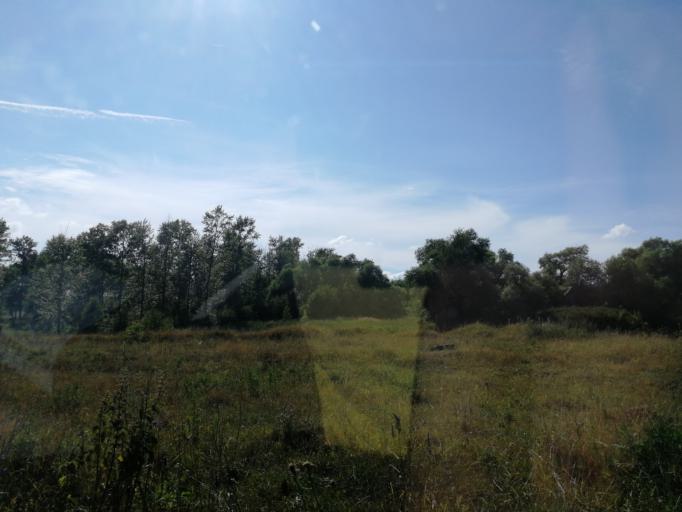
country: RU
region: Tula
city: Tovarkovskiy
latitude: 53.6094
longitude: 38.2723
